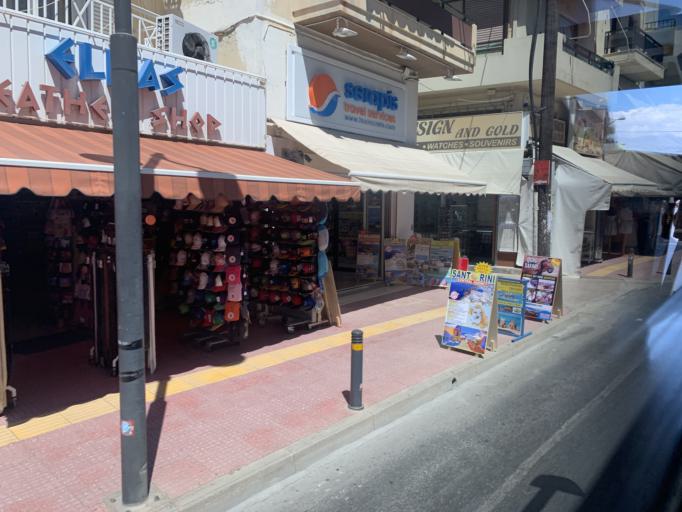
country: GR
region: Crete
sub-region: Nomos Irakleiou
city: Limin Khersonisou
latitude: 35.3156
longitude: 25.3931
